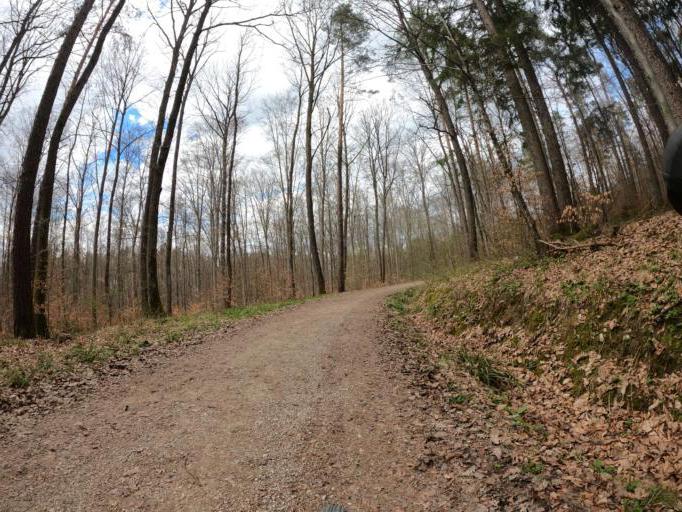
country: DE
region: Baden-Wuerttemberg
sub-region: Tuebingen Region
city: Gomaringen
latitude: 48.4380
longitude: 9.1144
